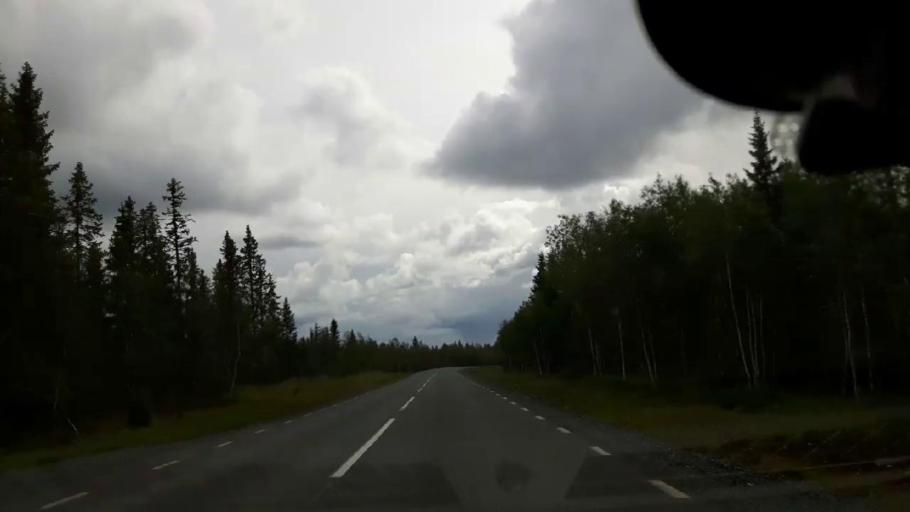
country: SE
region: Jaemtland
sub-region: Krokoms Kommun
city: Valla
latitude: 63.4570
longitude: 13.8285
